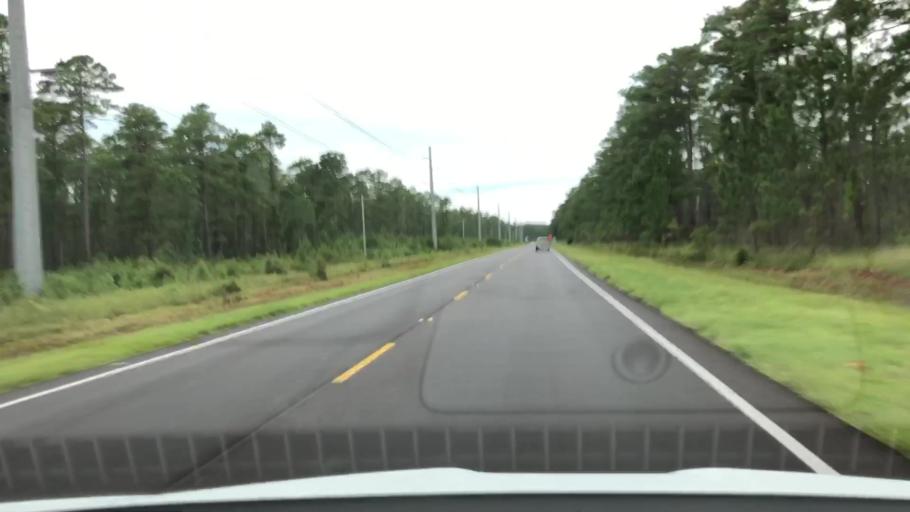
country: US
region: North Carolina
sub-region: Onslow County
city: Swansboro
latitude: 34.8109
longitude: -77.1371
